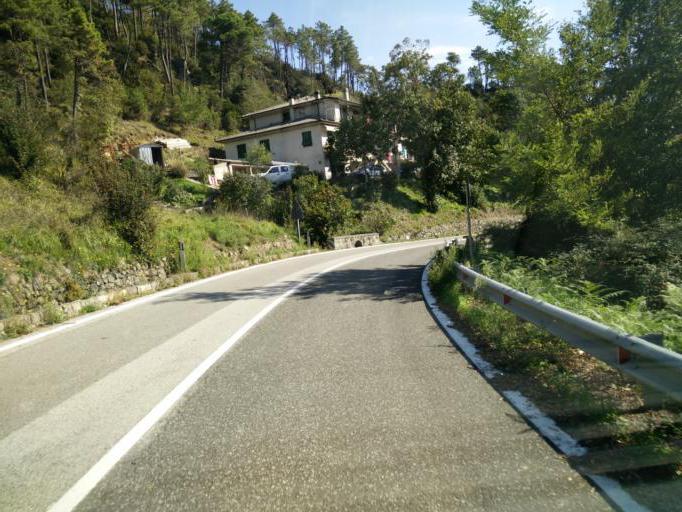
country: IT
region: Liguria
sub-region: Provincia di La Spezia
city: Carrodano
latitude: 44.2484
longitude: 9.6132
